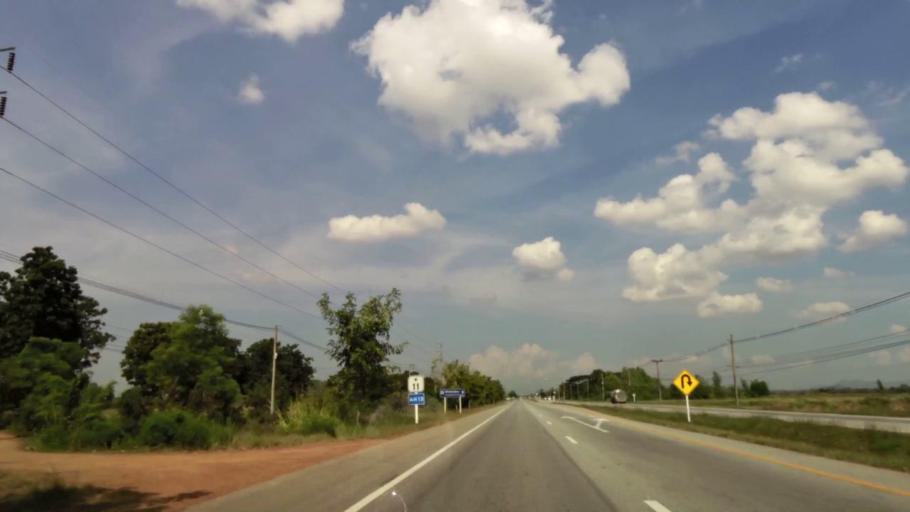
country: TH
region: Uttaradit
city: Thong Saen Khan
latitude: 17.4788
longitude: 100.2352
